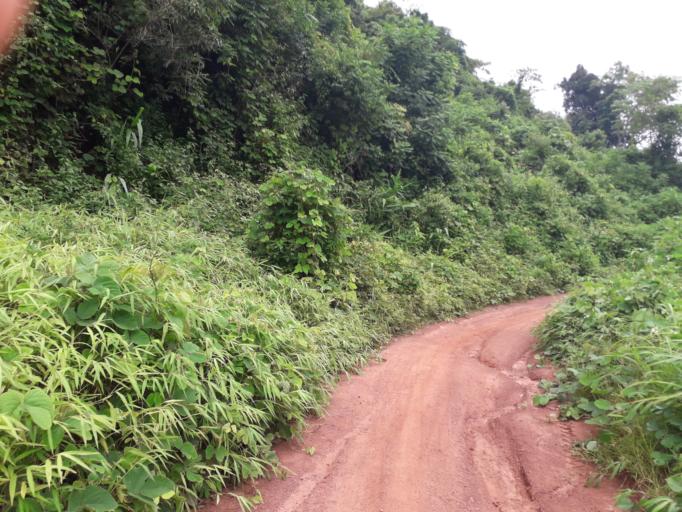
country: CN
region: Yunnan
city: Menglie
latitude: 22.2242
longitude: 101.6421
